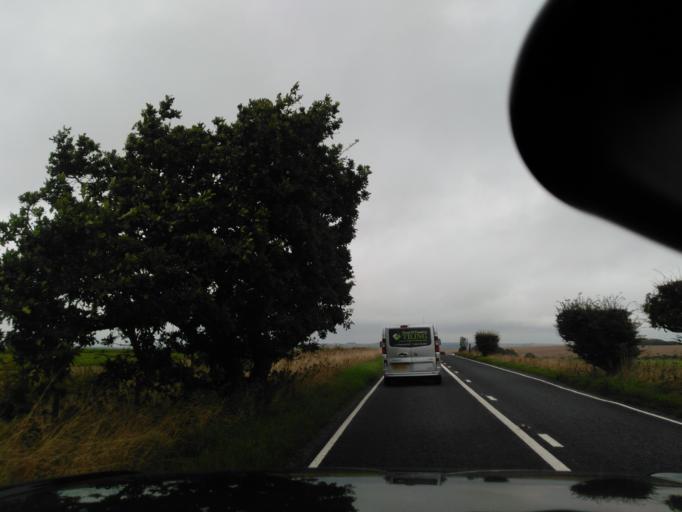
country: GB
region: England
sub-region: Wiltshire
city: Chicklade
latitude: 51.1381
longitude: -2.1623
